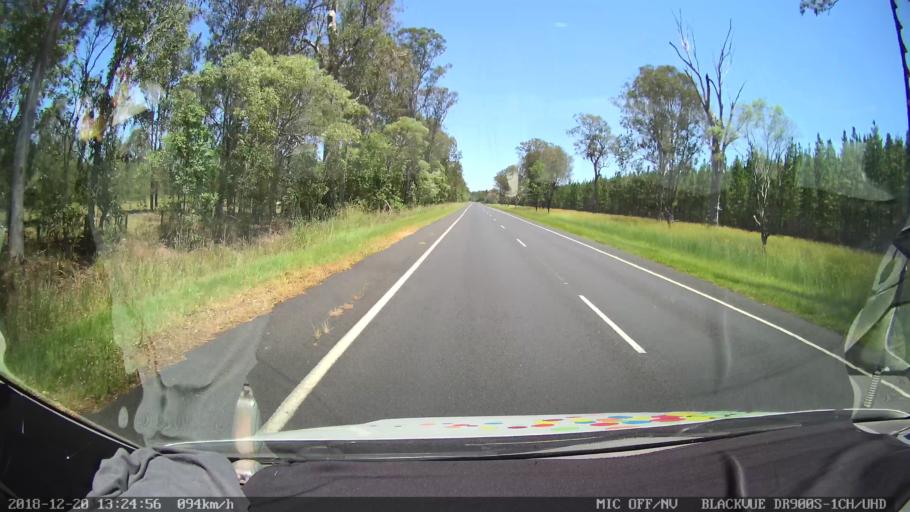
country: AU
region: New South Wales
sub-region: Richmond Valley
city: Casino
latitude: -29.1241
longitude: 152.9983
